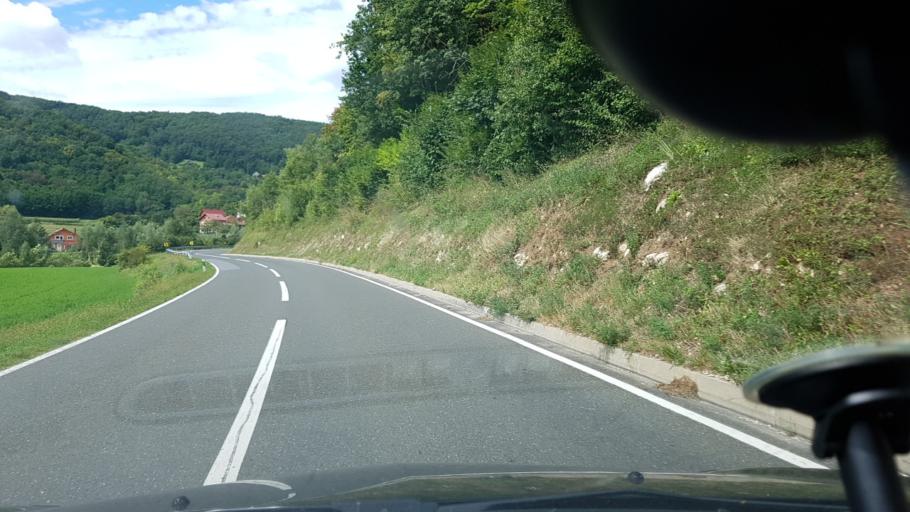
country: HR
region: Varazdinska
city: Lepoglava
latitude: 46.2138
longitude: 15.9978
